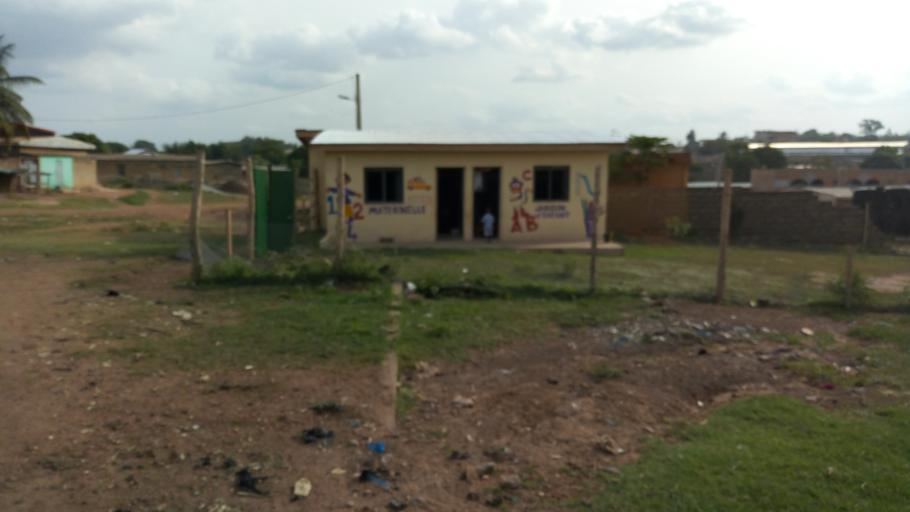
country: CI
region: Vallee du Bandama
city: Bouake
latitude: 7.7156
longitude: -5.0380
